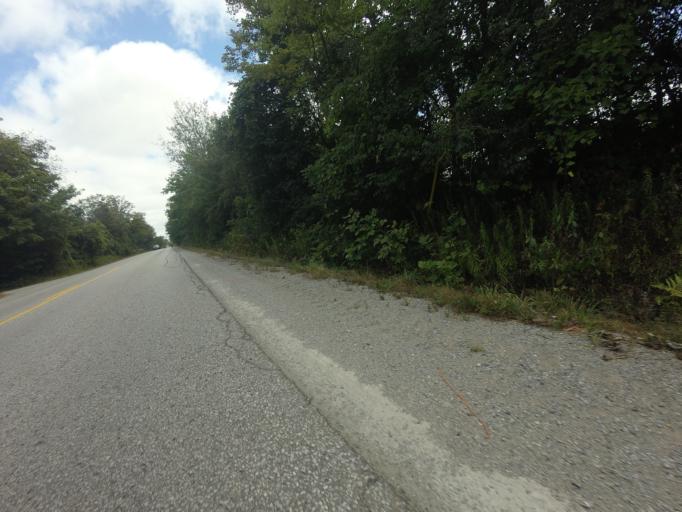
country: CA
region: Ontario
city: Uxbridge
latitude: 44.1198
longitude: -79.1921
